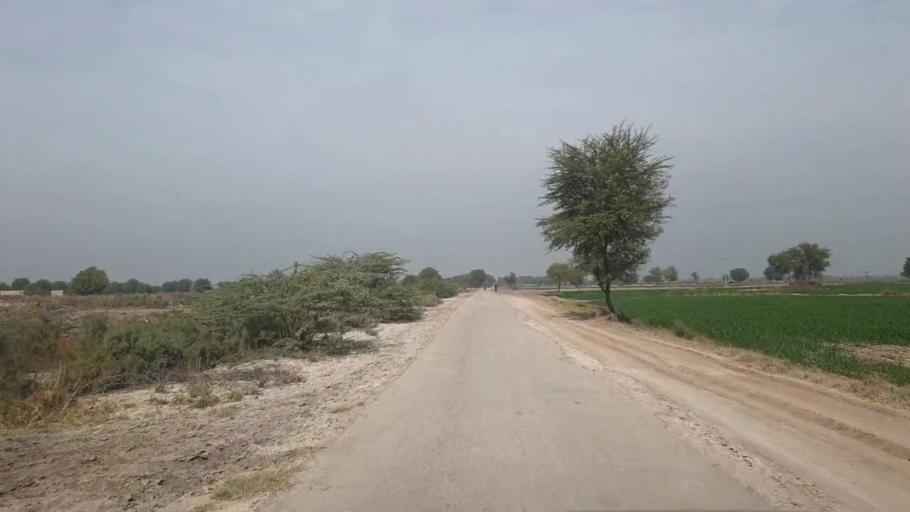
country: PK
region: Sindh
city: Nawabshah
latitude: 26.1153
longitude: 68.4800
